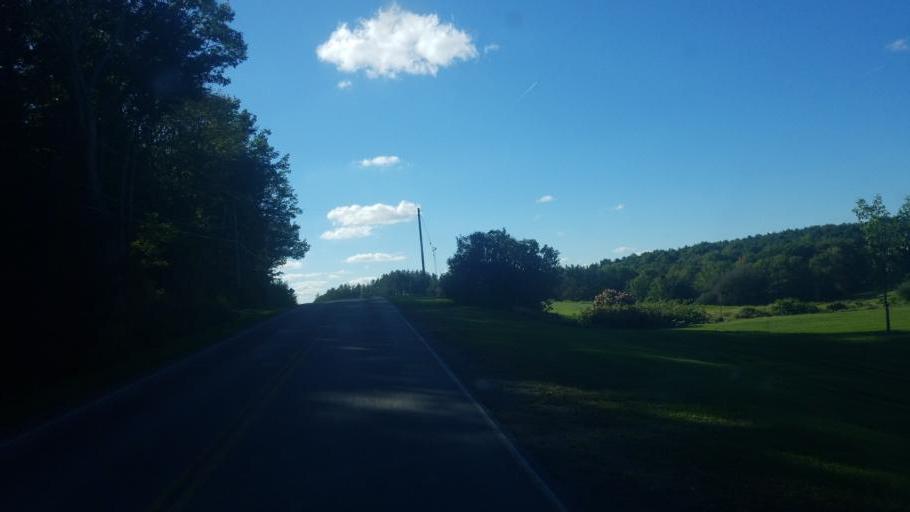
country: US
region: New York
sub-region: Allegany County
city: Friendship
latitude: 42.2775
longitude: -78.1727
